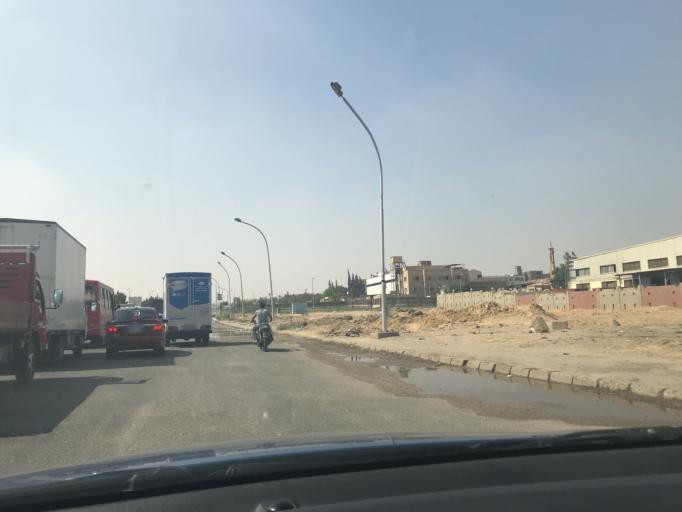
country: EG
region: Eastern Province
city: Bilbays
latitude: 30.2575
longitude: 31.7568
